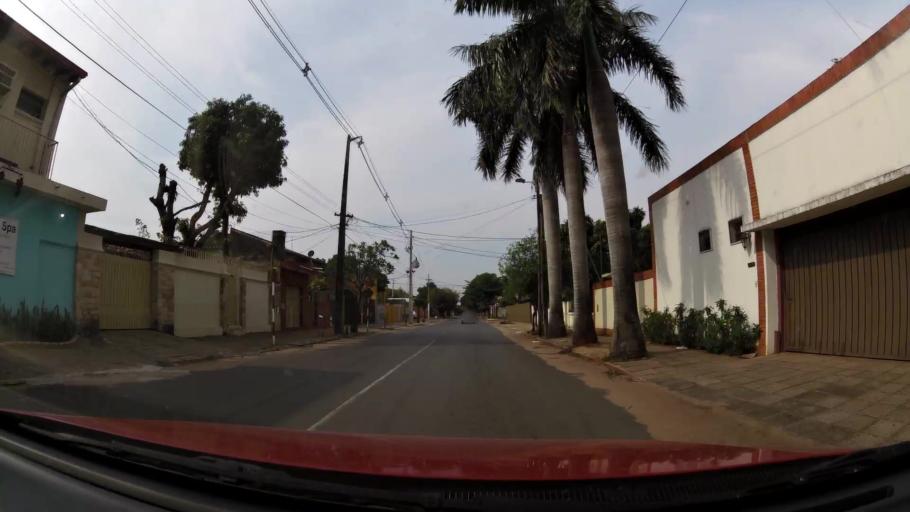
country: PY
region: Central
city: Fernando de la Mora
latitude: -25.2998
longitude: -57.5564
